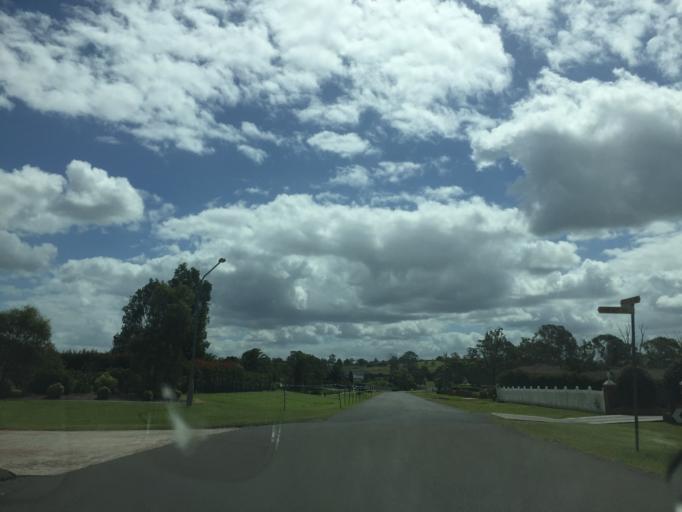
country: AU
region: New South Wales
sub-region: Penrith Municipality
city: Kingswood Park
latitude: -33.7958
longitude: 150.7458
